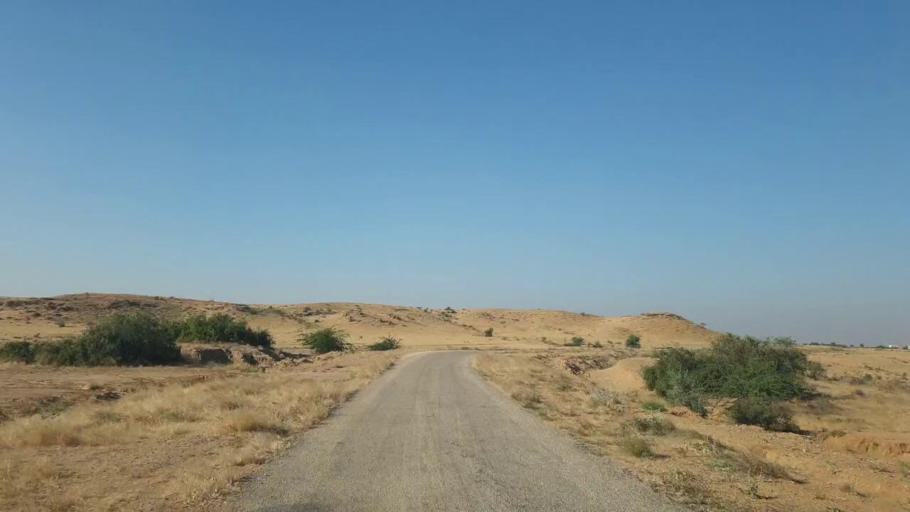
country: PK
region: Sindh
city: Malir Cantonment
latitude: 25.4137
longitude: 67.4639
